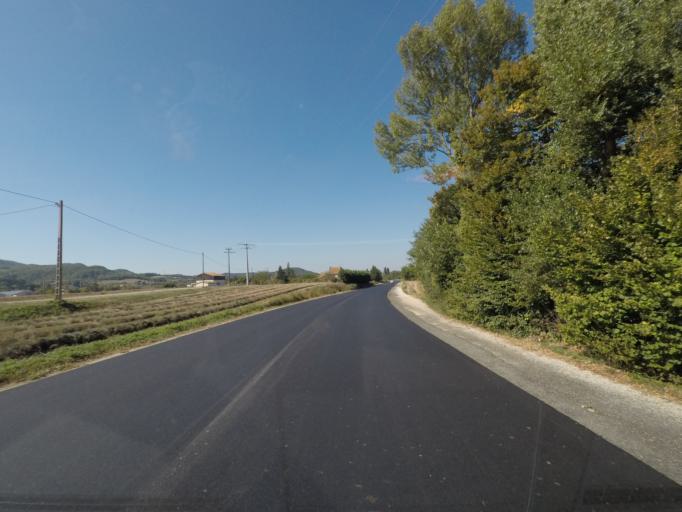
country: FR
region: Rhone-Alpes
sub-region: Departement de la Drome
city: Aouste-sur-Sye
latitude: 44.7039
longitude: 5.1048
